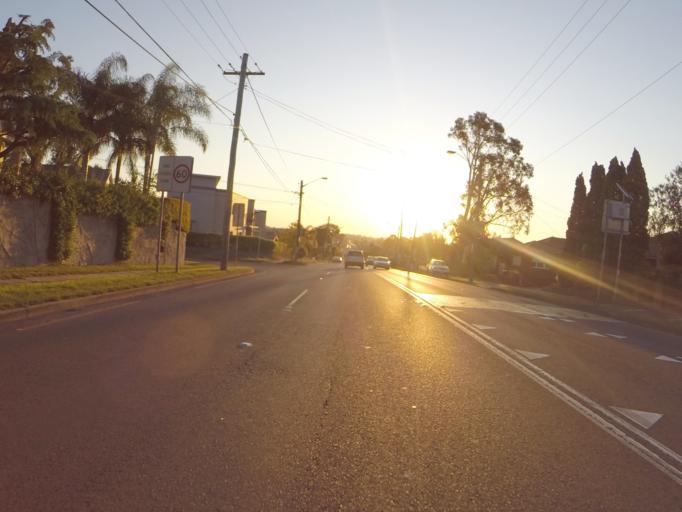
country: AU
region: New South Wales
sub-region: Hurstville
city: Earlwood
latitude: -33.9503
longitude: 151.0976
